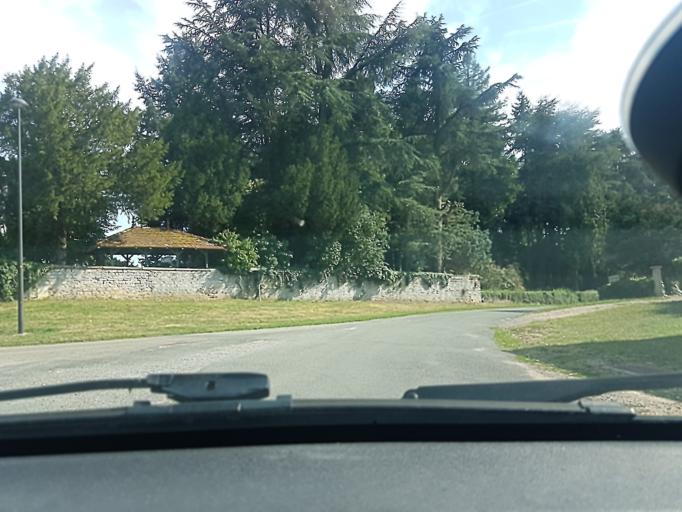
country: FR
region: Bourgogne
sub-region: Departement de Saone-et-Loire
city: Epervans
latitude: 46.7486
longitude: 4.9014
